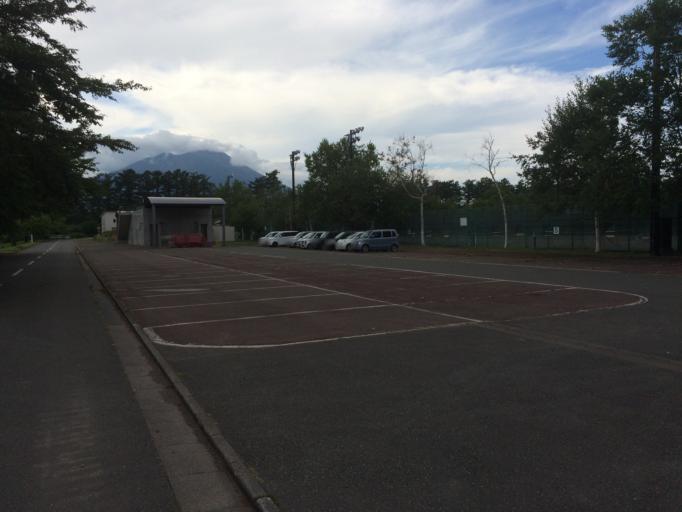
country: JP
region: Iwate
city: Morioka-shi
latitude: 39.8028
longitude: 141.1344
